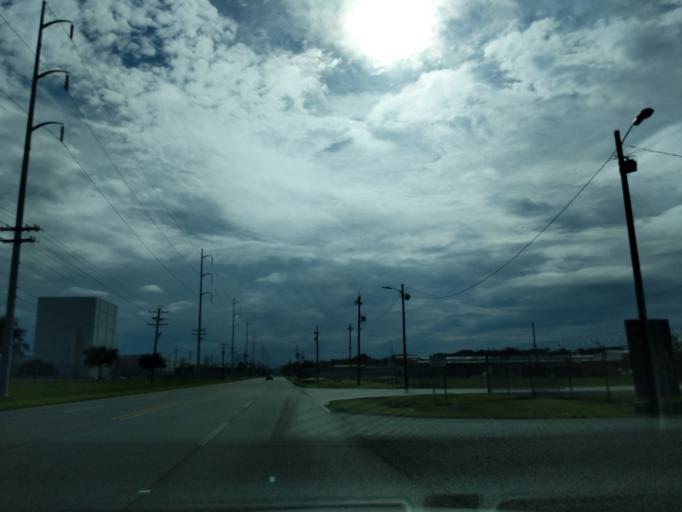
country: US
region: Louisiana
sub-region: Saint Bernard Parish
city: Chalmette
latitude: 30.0313
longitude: -89.9123
